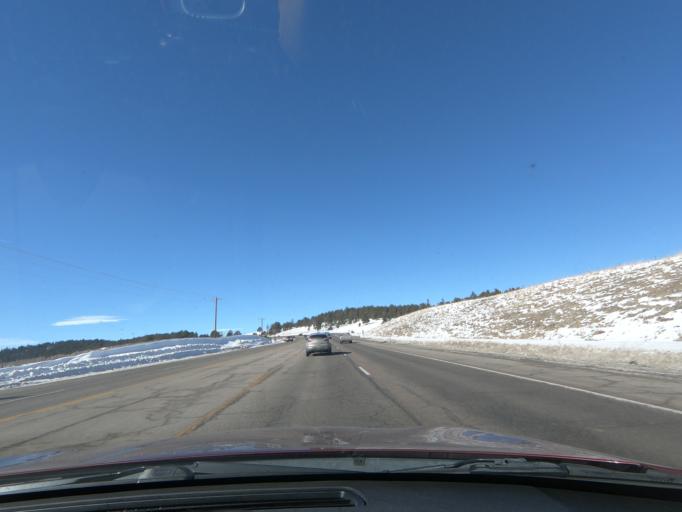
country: US
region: Colorado
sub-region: Teller County
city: Woodland Park
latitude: 38.9578
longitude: -105.1067
